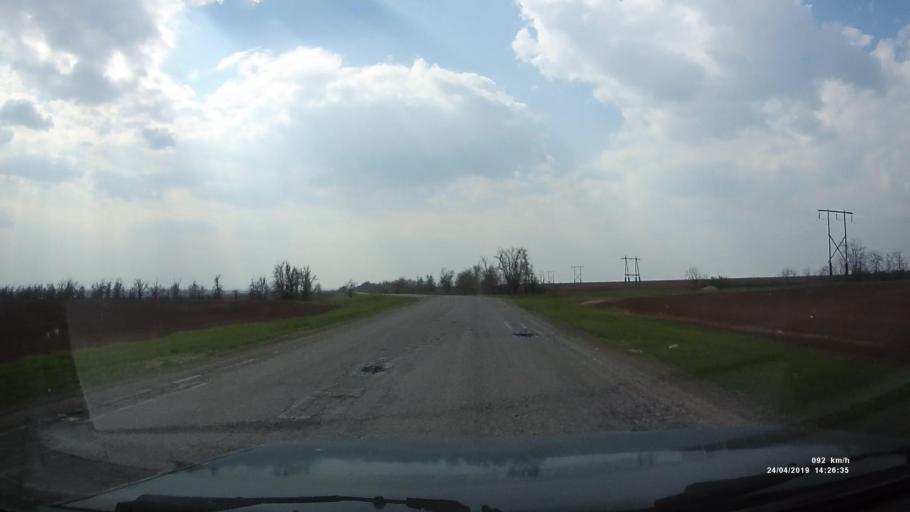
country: RU
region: Kalmykiya
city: Arshan'
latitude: 46.3343
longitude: 44.0600
